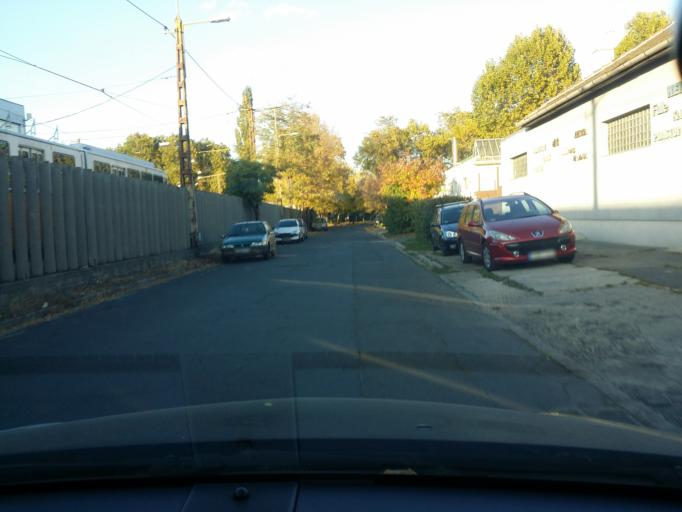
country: HU
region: Budapest
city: Budapest IV. keruelet
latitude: 47.5515
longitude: 19.0937
